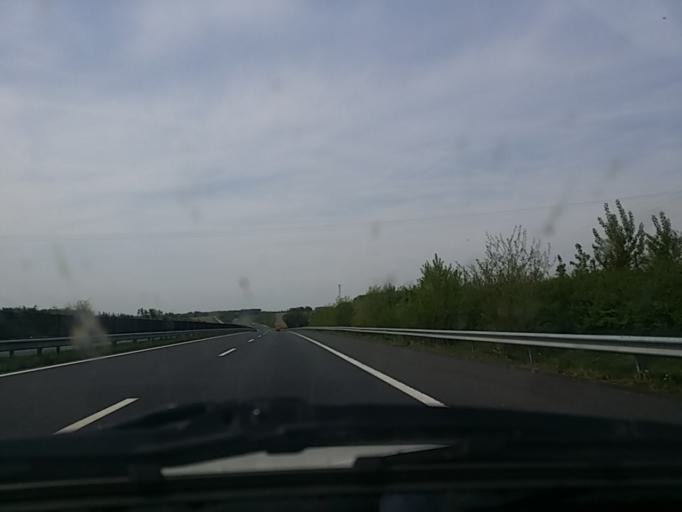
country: HU
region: Zala
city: Zalakomar
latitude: 46.4853
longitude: 17.0961
